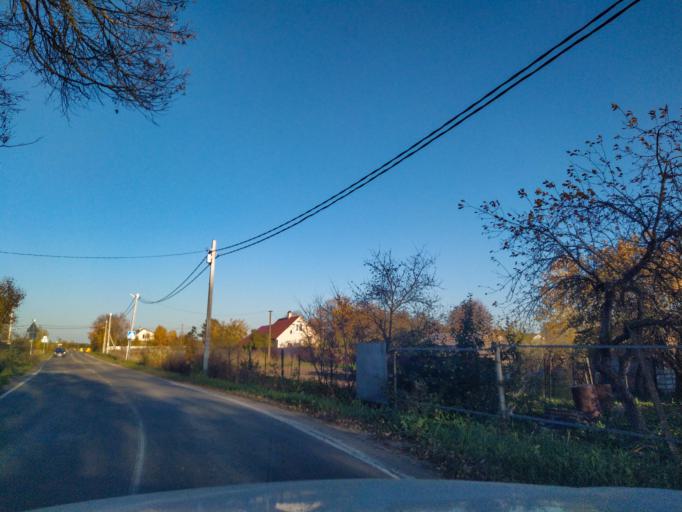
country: RU
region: Leningrad
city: Siverskiy
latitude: 59.3283
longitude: 30.0395
